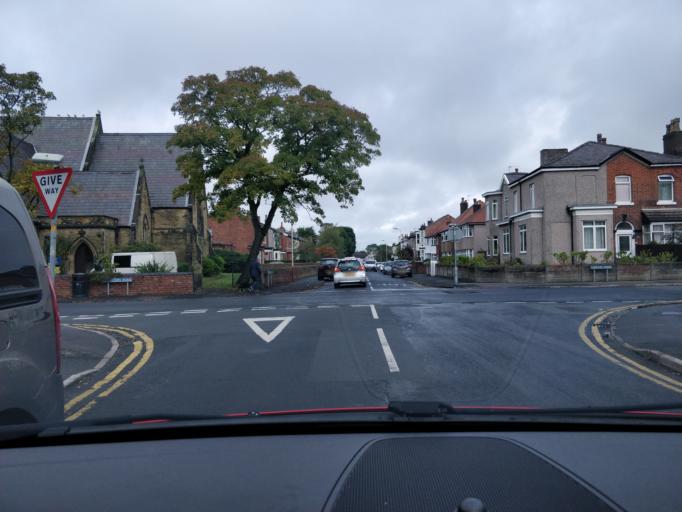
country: GB
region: England
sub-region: Sefton
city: Southport
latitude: 53.6318
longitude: -3.0093
